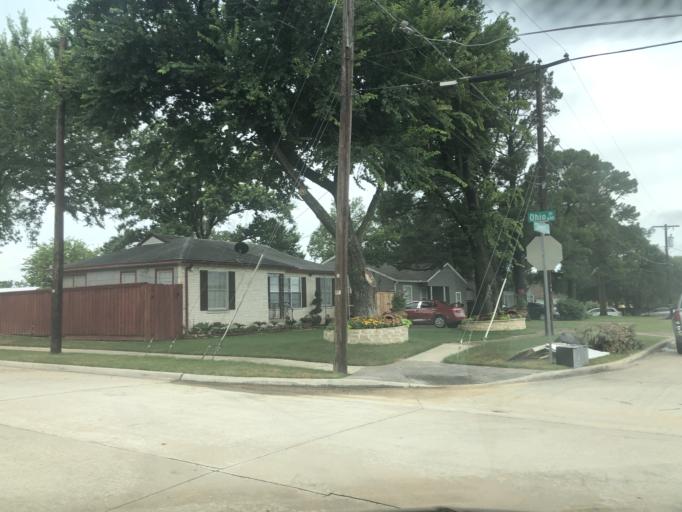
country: US
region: Texas
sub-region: Dallas County
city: Irving
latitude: 32.8075
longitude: -96.9490
